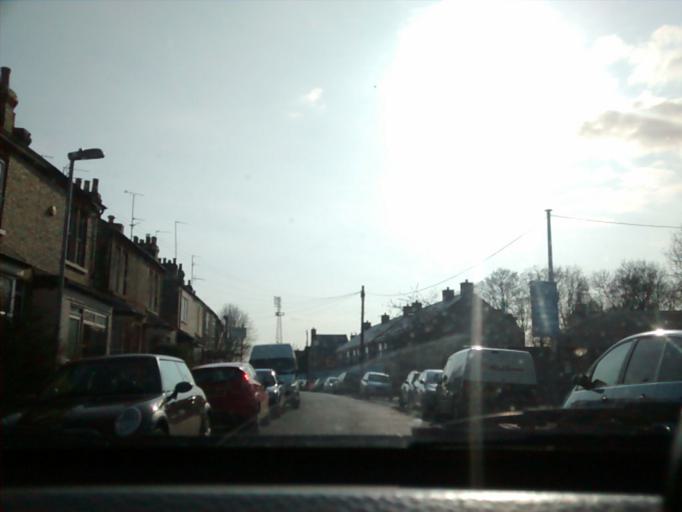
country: GB
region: England
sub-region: Cambridgeshire
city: Cambridge
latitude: 52.2148
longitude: 0.1555
